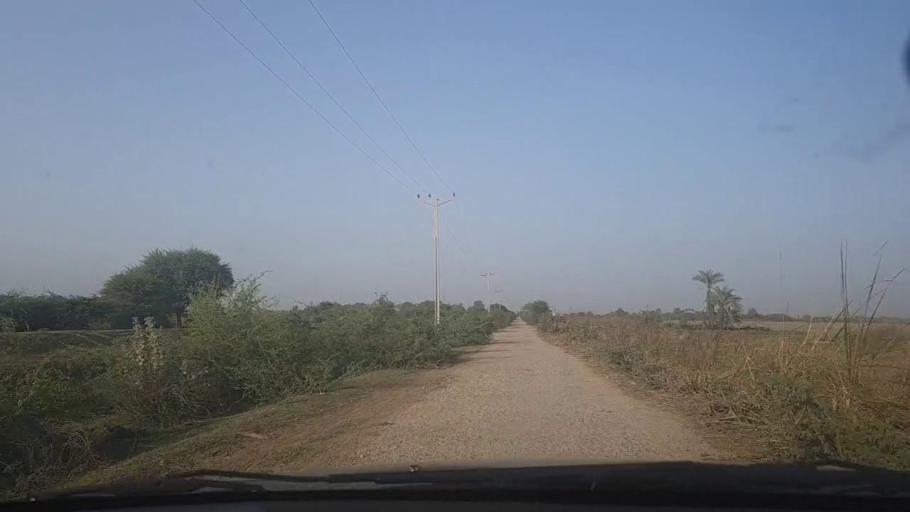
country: PK
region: Sindh
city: Keti Bandar
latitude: 24.2856
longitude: 67.6033
